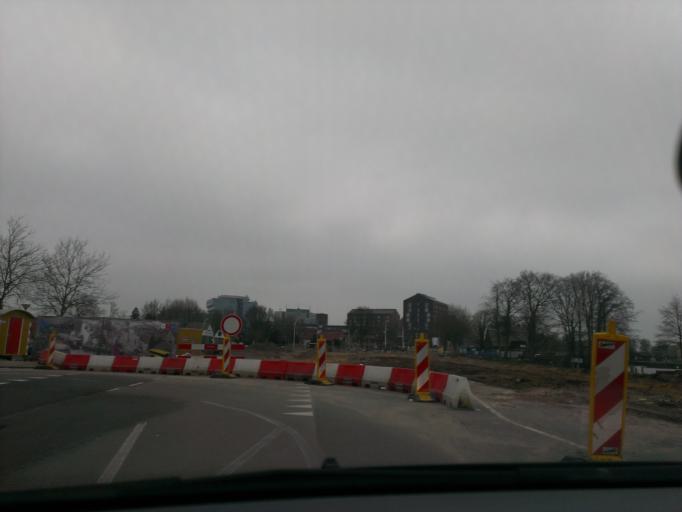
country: NL
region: Overijssel
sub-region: Gemeente Zwolle
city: Zwolle
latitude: 52.5126
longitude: 6.0868
